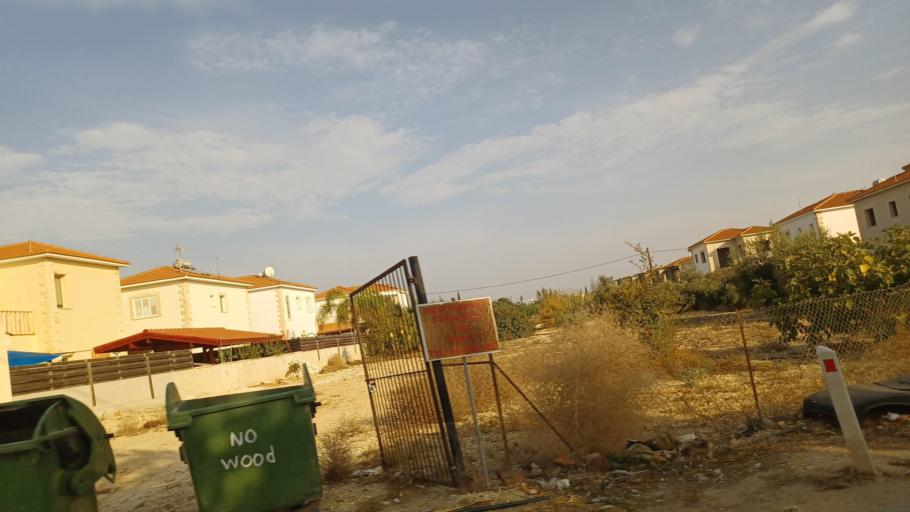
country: CY
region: Ammochostos
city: Acheritou
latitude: 35.0759
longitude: 33.8742
